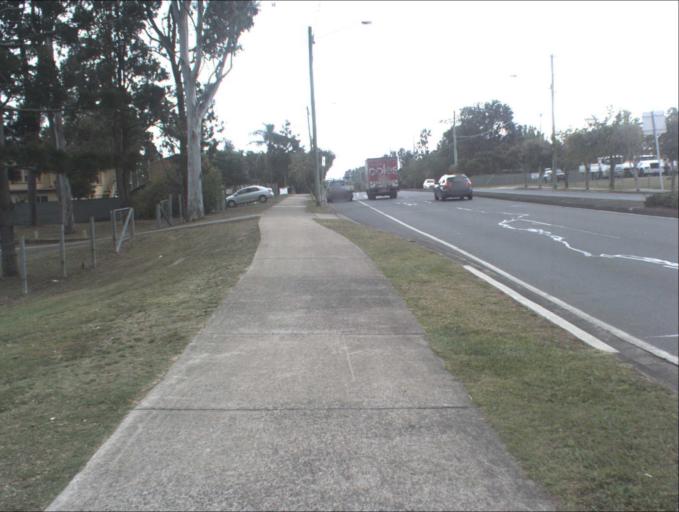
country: AU
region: Queensland
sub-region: Logan
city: Waterford West
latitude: -27.6812
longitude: 153.1372
